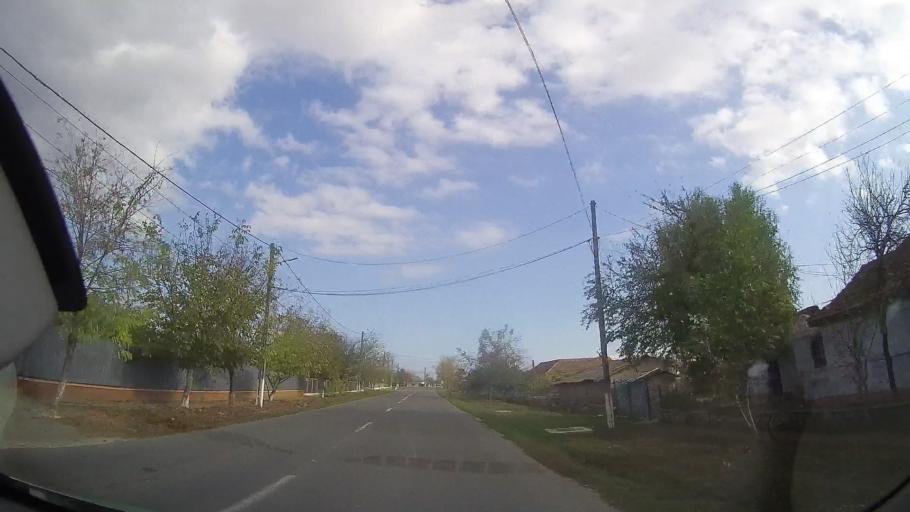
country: RO
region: Constanta
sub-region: Comuna Pecineaga
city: Pecineaga
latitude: 43.8950
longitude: 28.5079
